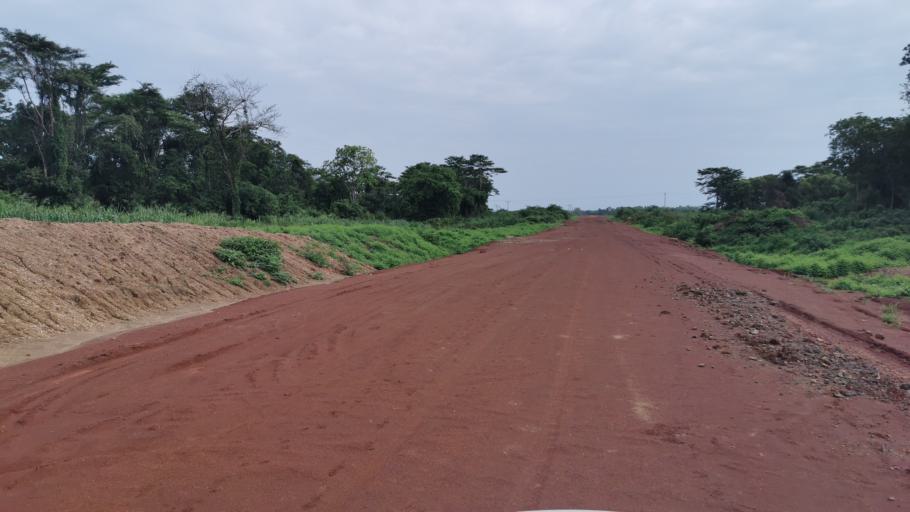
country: ET
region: Gambela
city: Gambela
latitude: 7.8657
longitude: 34.4930
